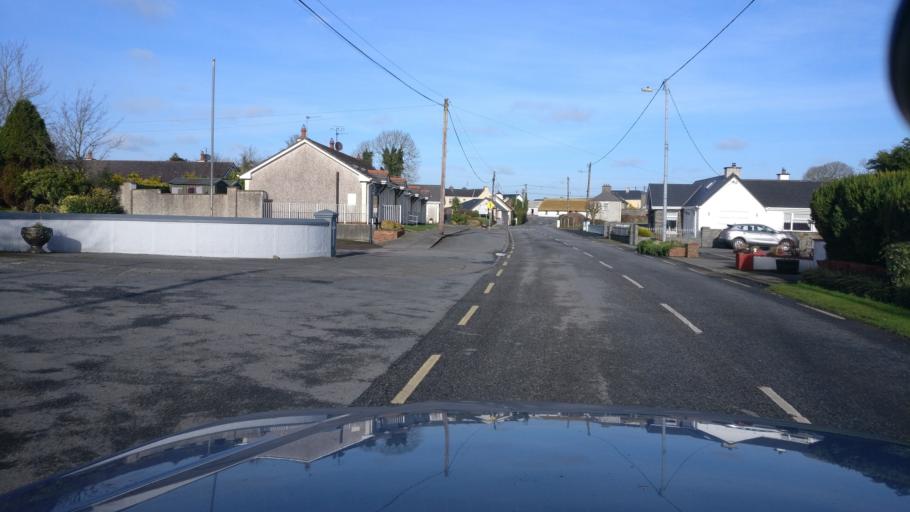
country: IE
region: Leinster
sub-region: Kilkenny
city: Castlecomer
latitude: 52.8589
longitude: -7.1640
